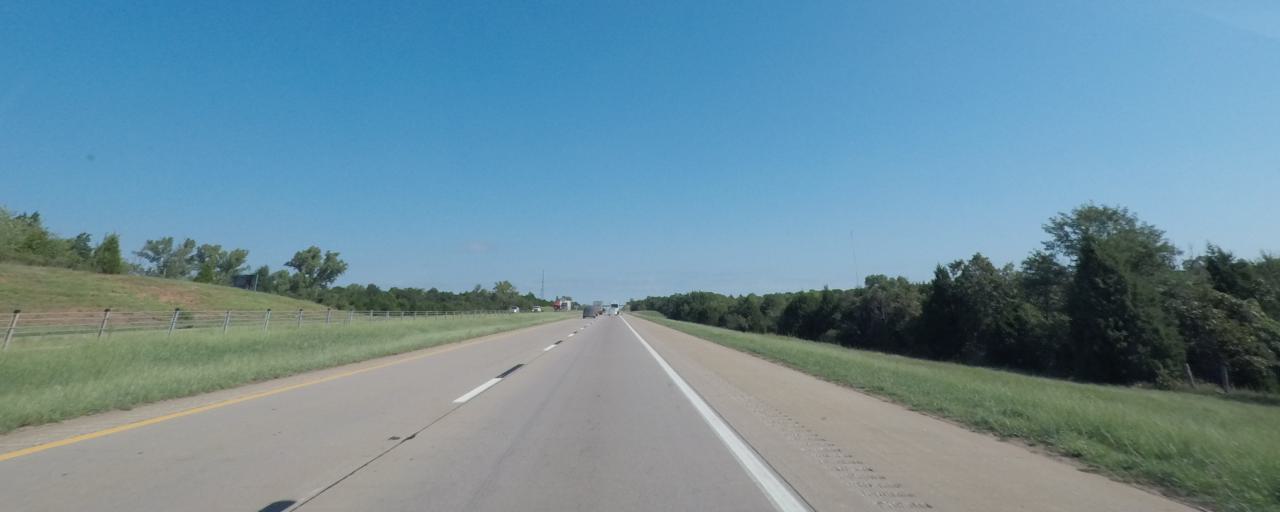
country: US
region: Oklahoma
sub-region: Oklahoma County
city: Edmond
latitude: 35.7454
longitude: -97.4162
